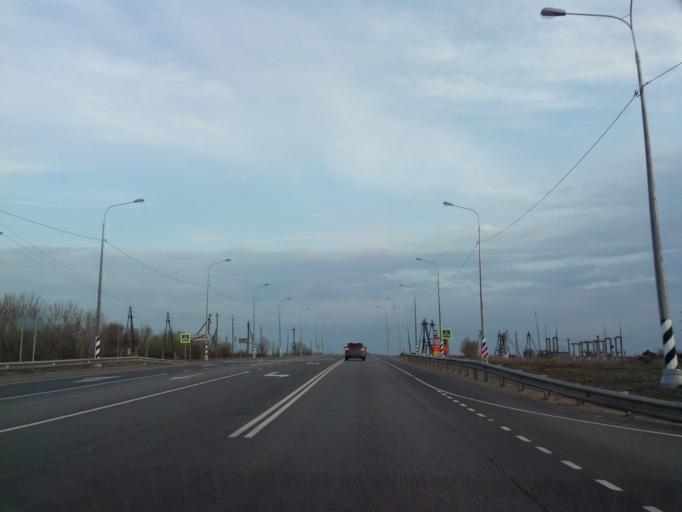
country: RU
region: Rjazan
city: Ryazhsk
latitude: 53.5910
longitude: 40.0376
